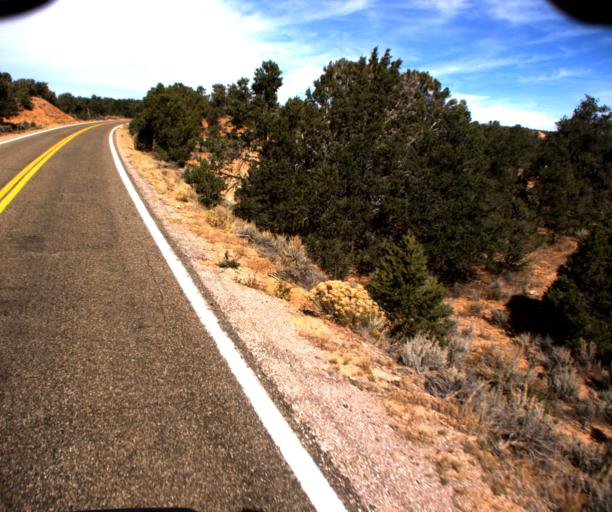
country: US
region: Arizona
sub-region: Navajo County
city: Kayenta
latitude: 36.6193
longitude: -110.5065
